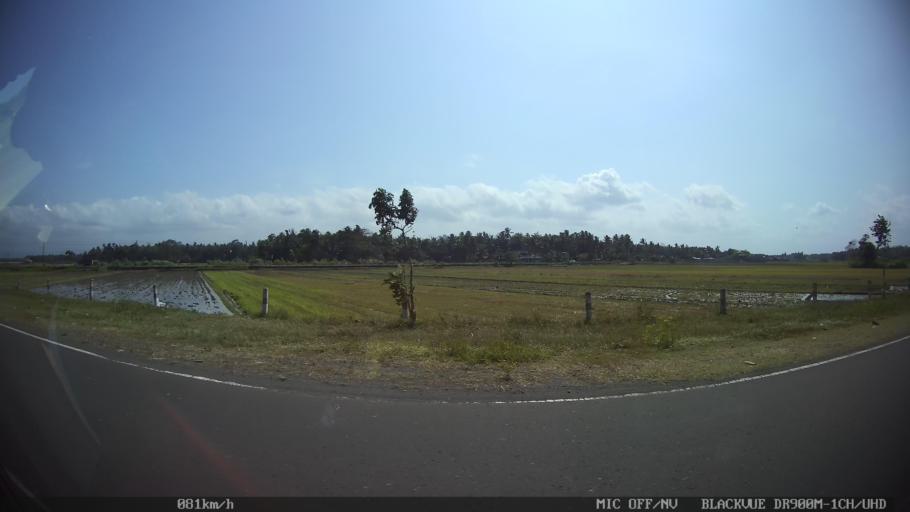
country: ID
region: Daerah Istimewa Yogyakarta
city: Srandakan
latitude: -7.9540
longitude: 110.1956
